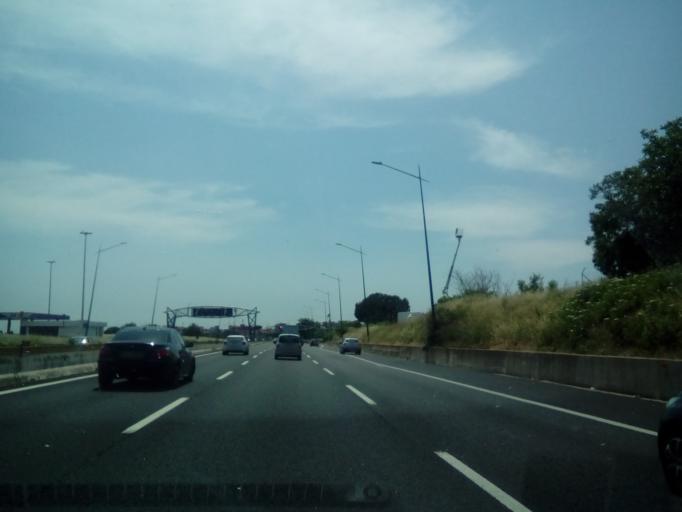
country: IT
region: Latium
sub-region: Citta metropolitana di Roma Capitale
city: Valle Santa
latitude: 41.9604
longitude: 12.3901
